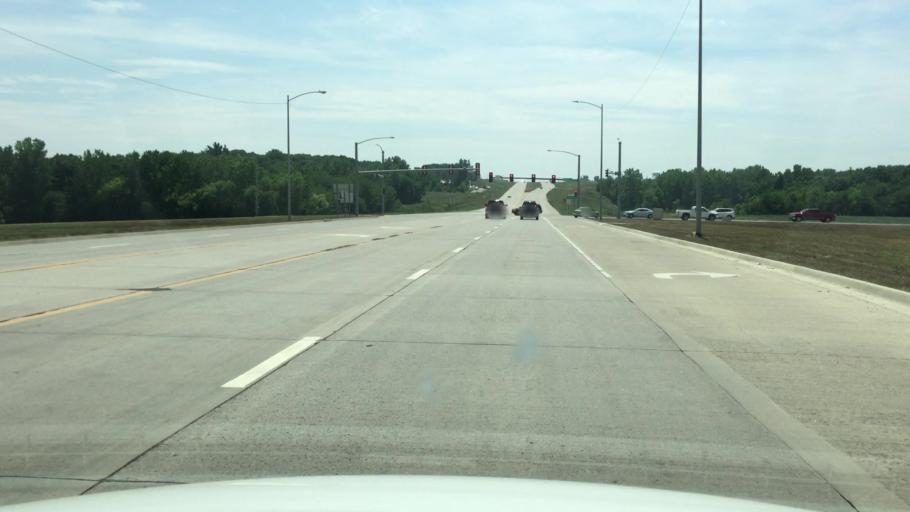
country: US
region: Kansas
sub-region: Jackson County
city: Holton
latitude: 39.4571
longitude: -95.7480
